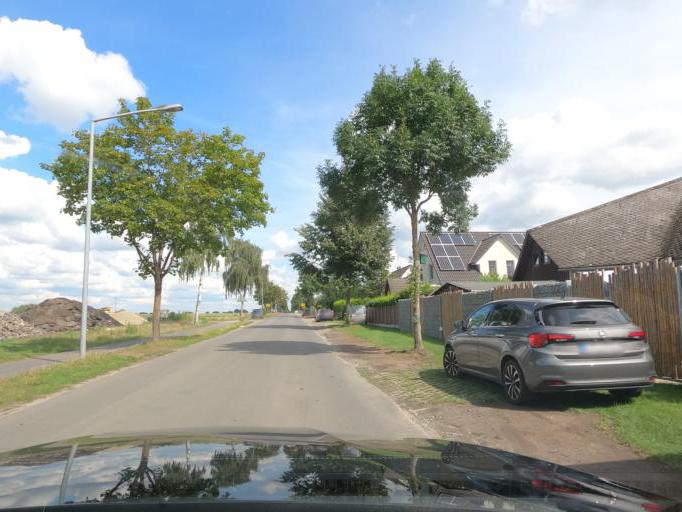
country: DE
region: Lower Saxony
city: Isernhagen Farster Bauerschaft
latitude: 52.4991
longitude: 9.8679
